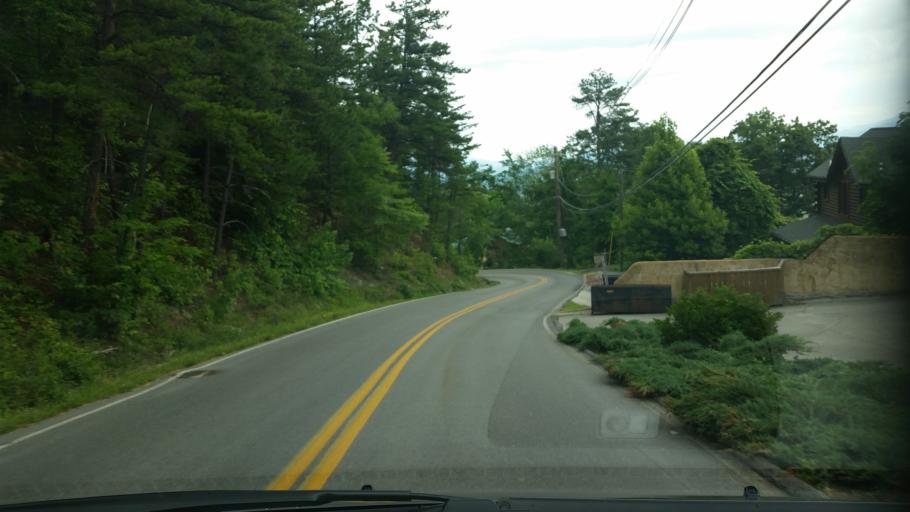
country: US
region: Tennessee
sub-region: Sevier County
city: Gatlinburg
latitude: 35.7087
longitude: -83.5575
